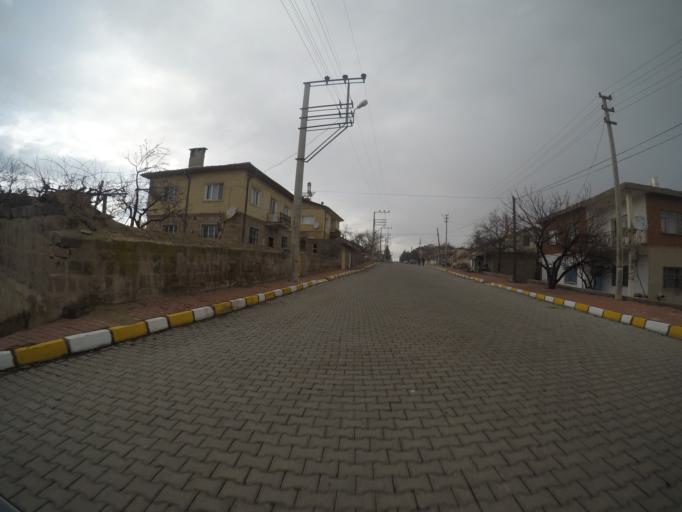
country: TR
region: Nevsehir
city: Goereme
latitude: 38.6281
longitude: 34.8593
